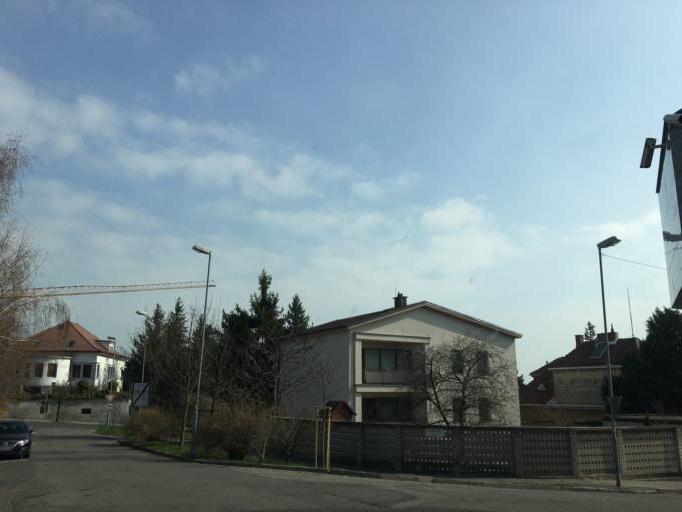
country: SK
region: Bratislavsky
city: Bratislava
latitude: 48.1456
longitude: 17.0911
